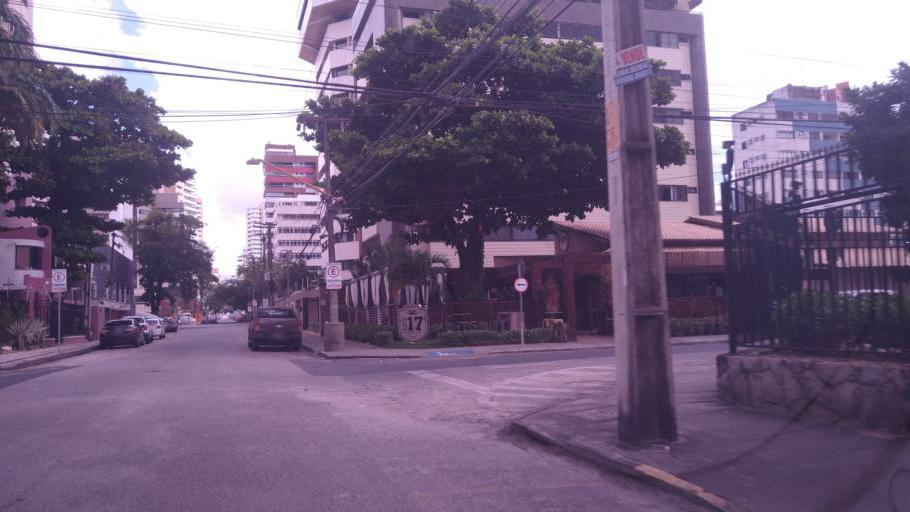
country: BR
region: Ceara
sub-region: Fortaleza
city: Fortaleza
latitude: -3.7332
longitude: -38.4907
